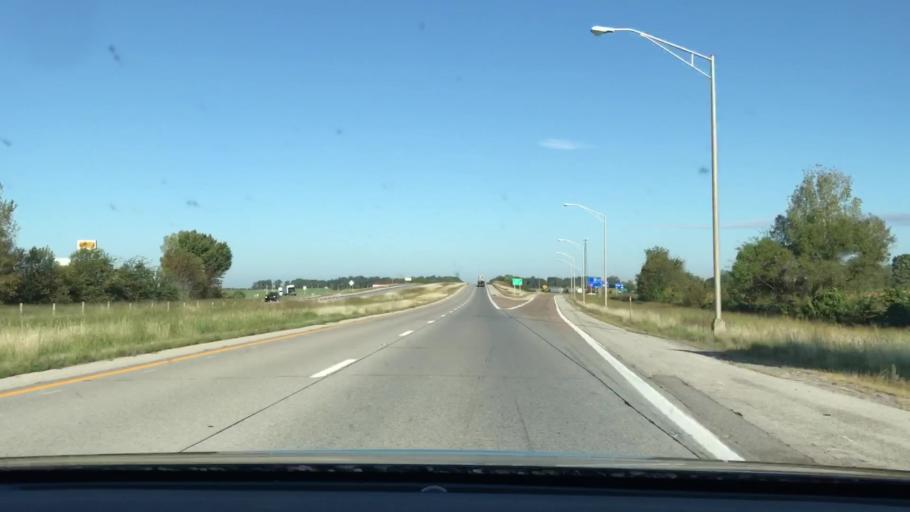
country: US
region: Kentucky
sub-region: Trigg County
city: Cadiz
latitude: 36.8793
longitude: -87.7307
